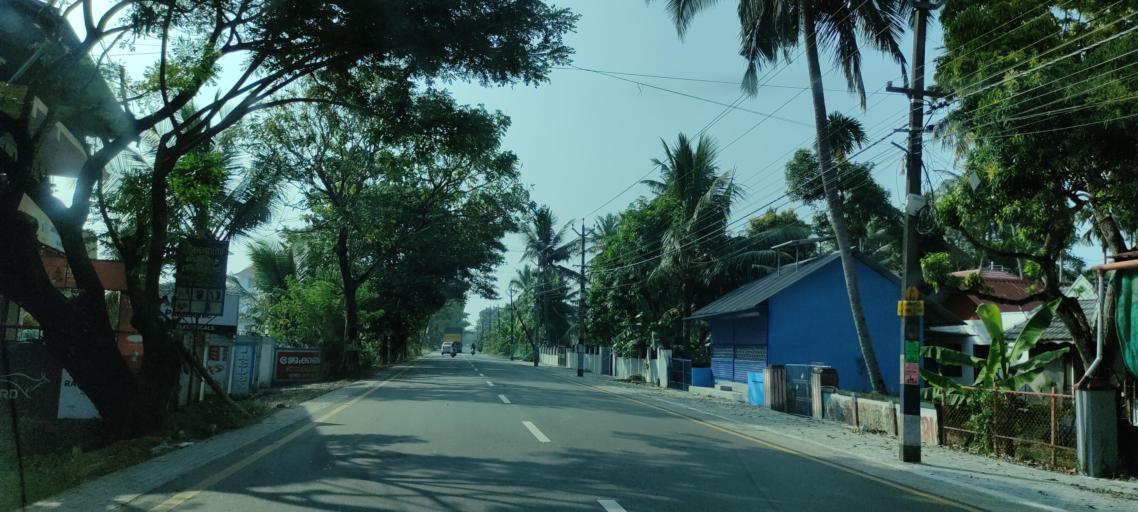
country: IN
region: Kerala
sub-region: Kottayam
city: Changanacheri
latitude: 9.3618
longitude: 76.4639
